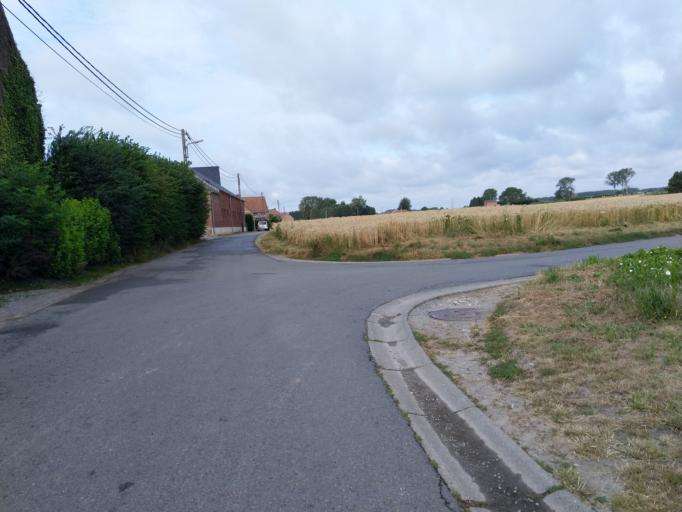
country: BE
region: Wallonia
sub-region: Province du Hainaut
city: Lens
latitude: 50.5482
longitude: 3.8788
